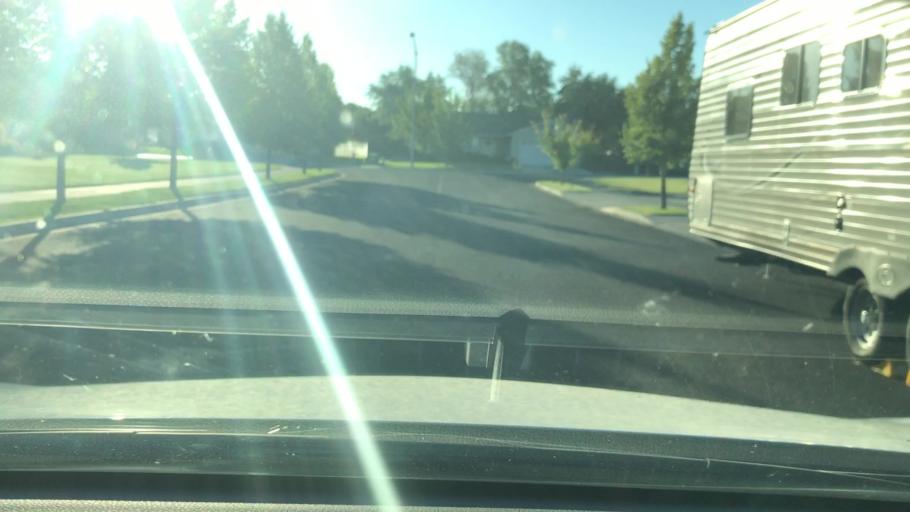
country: US
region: Washington
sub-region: Grant County
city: Moses Lake
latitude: 47.1199
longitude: -119.2531
